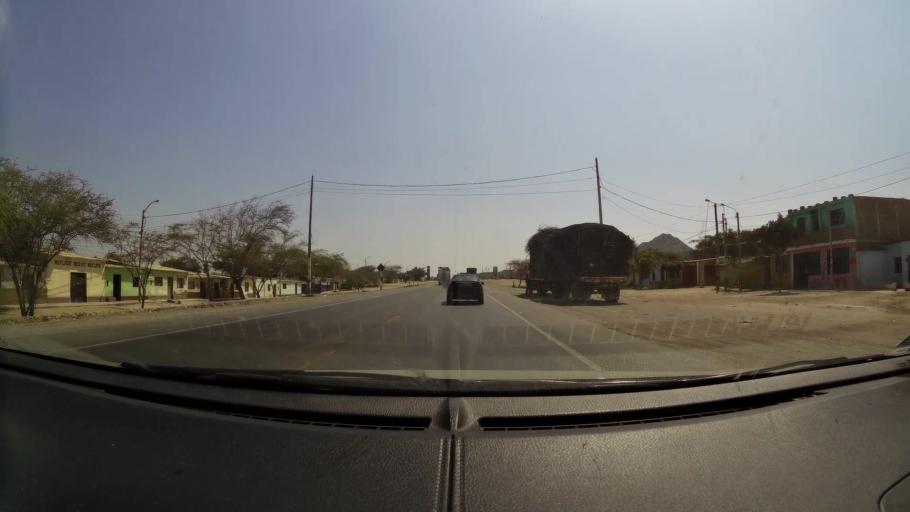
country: PE
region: Lambayeque
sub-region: Provincia de Chiclayo
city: Mocupe
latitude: -6.9785
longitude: -79.6490
